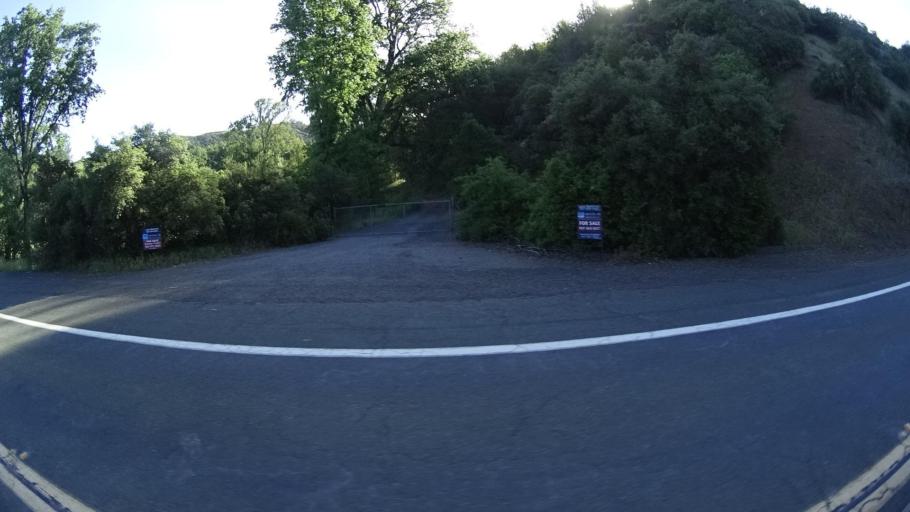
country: US
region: California
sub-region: Lake County
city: North Lakeport
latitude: 39.1051
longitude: -122.9710
